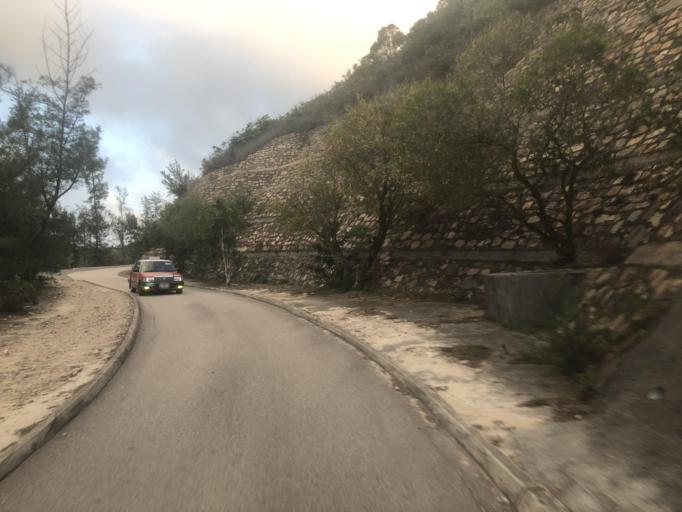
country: HK
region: Sai Kung
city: Sai Kung
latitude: 22.3664
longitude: 114.3468
